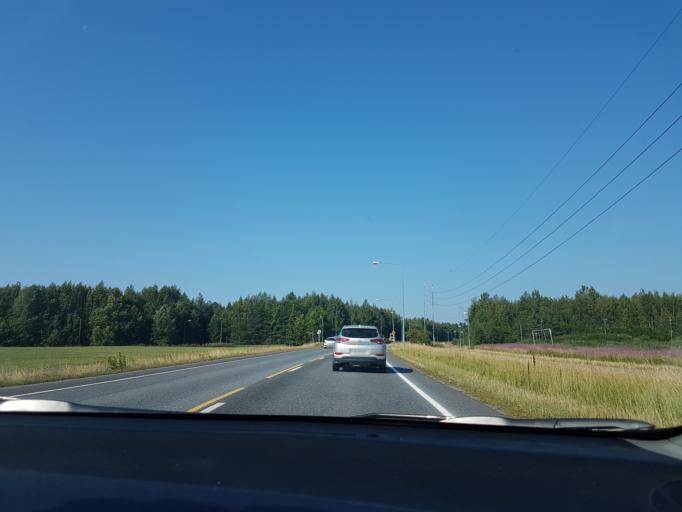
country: FI
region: Uusimaa
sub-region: Helsinki
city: Tuusula
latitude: 60.3726
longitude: 25.0408
